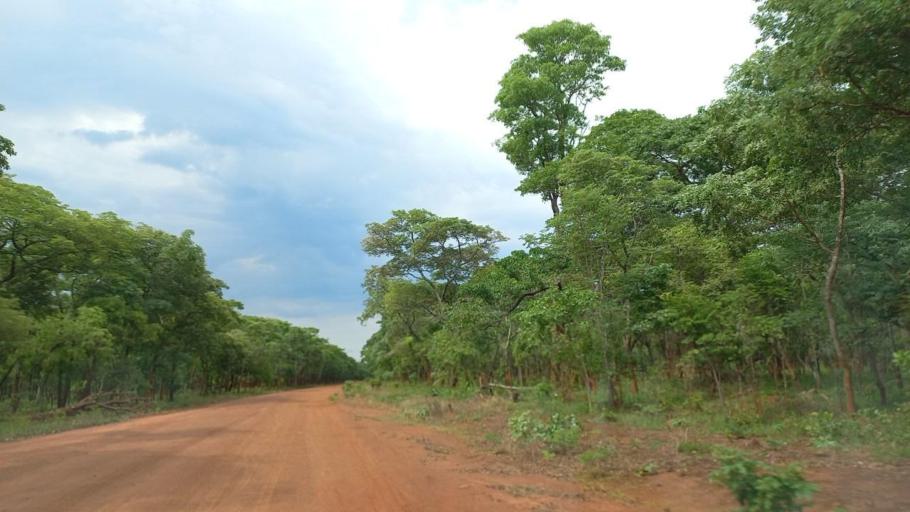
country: ZM
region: North-Western
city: Kalengwa
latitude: -13.4140
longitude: 25.0608
